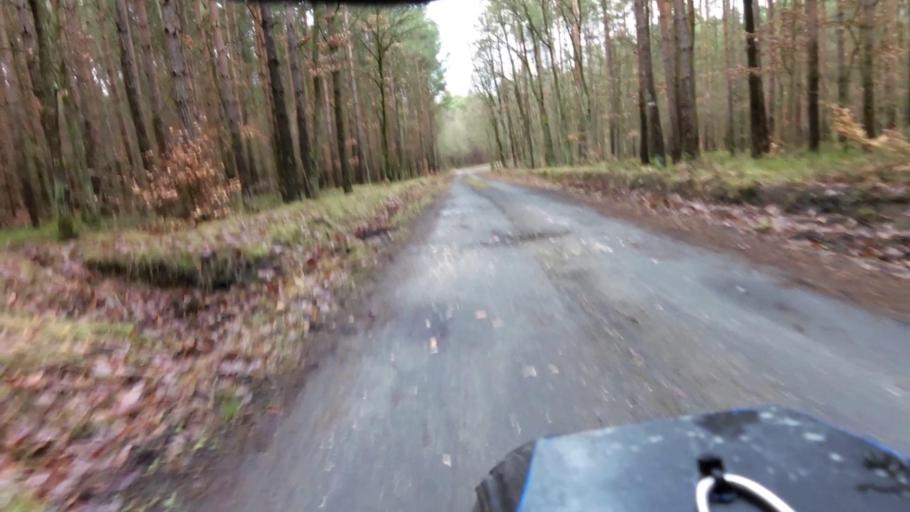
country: PL
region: Lubusz
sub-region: Powiat gorzowski
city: Bogdaniec
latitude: 52.6936
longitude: 15.0283
